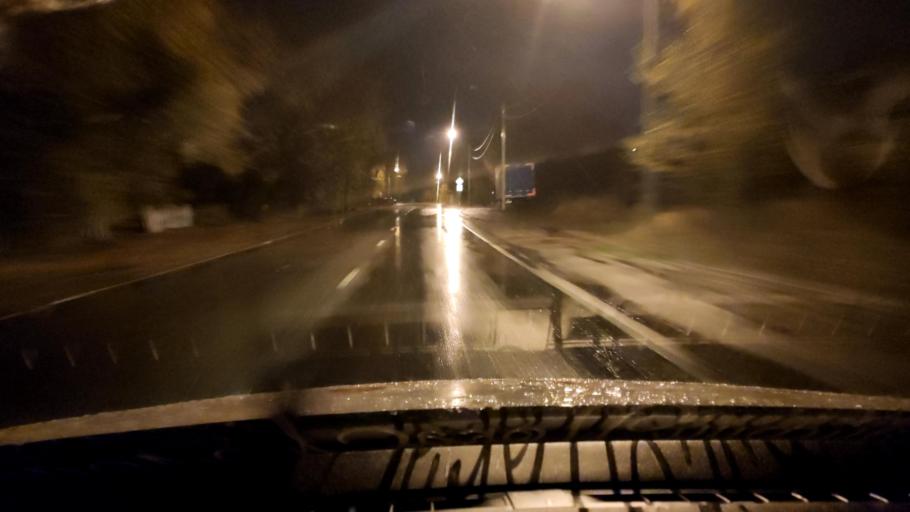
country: RU
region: Voronezj
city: Somovo
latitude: 51.7268
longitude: 39.2965
